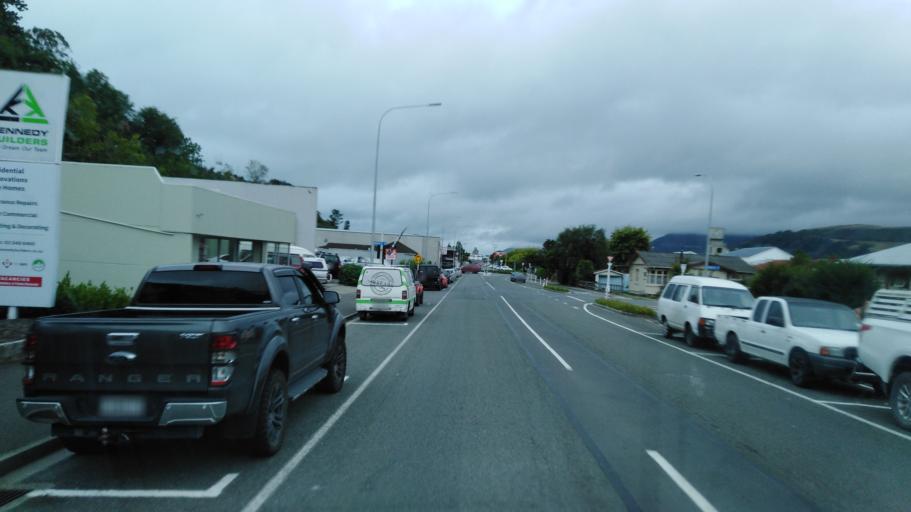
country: NZ
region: Nelson
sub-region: Nelson City
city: Nelson
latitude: -41.2749
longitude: 173.2750
